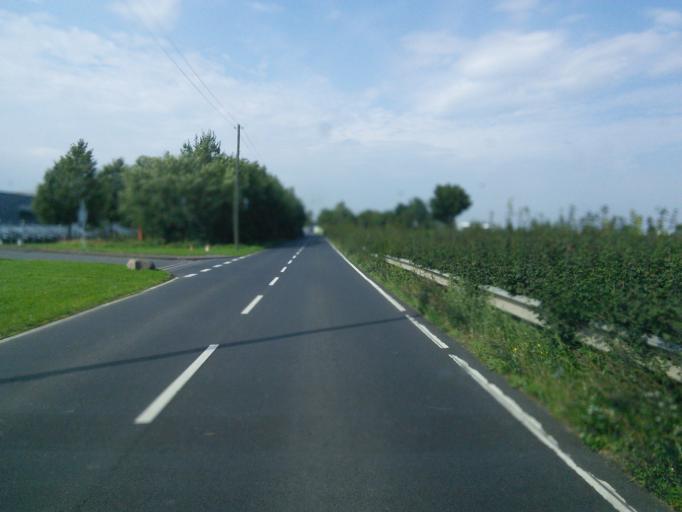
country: DE
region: North Rhine-Westphalia
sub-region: Regierungsbezirk Koln
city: Pulheim
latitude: 50.9629
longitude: 6.8196
